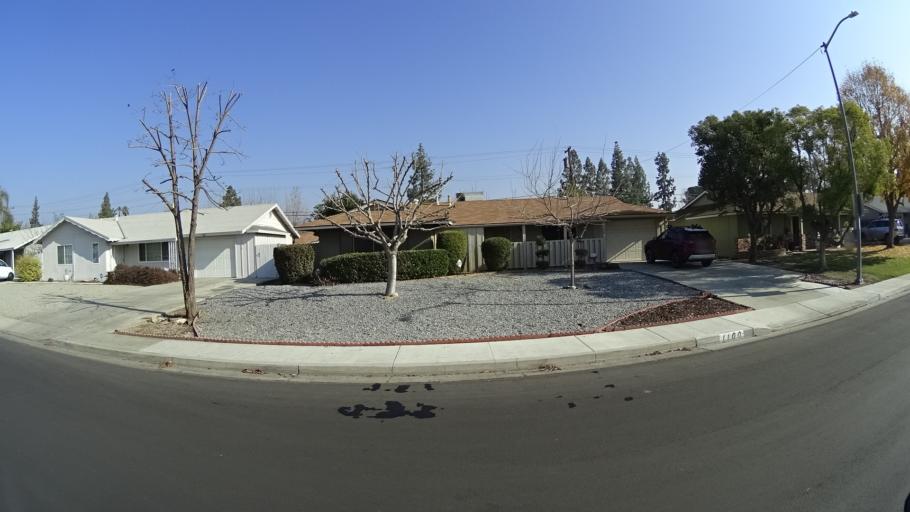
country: US
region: California
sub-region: Kern County
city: Bakersfield
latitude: 35.3449
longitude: -119.0621
